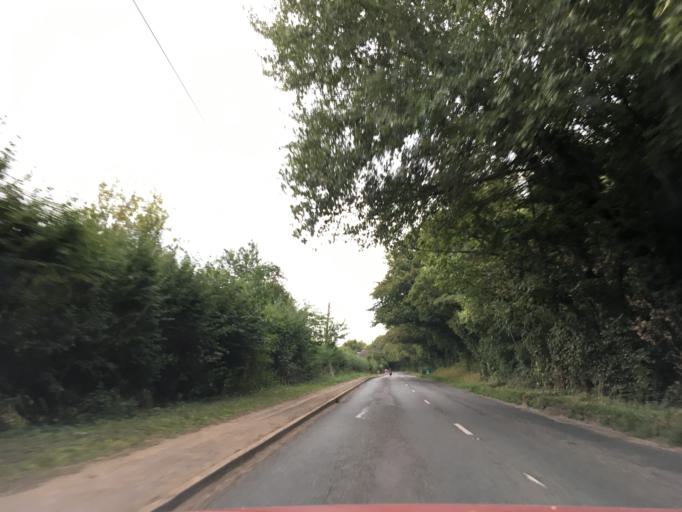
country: GB
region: England
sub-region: Wiltshire
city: Bremhill
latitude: 51.4289
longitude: -2.0628
